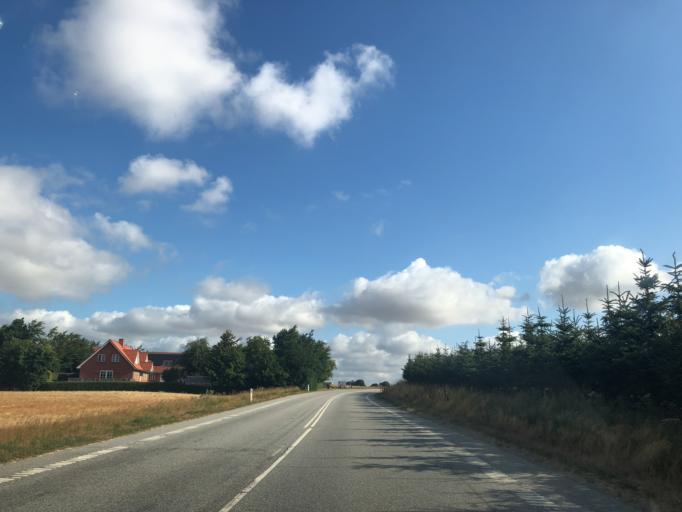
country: DK
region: Central Jutland
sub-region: Skive Kommune
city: Skive
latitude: 56.6242
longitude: 8.8829
